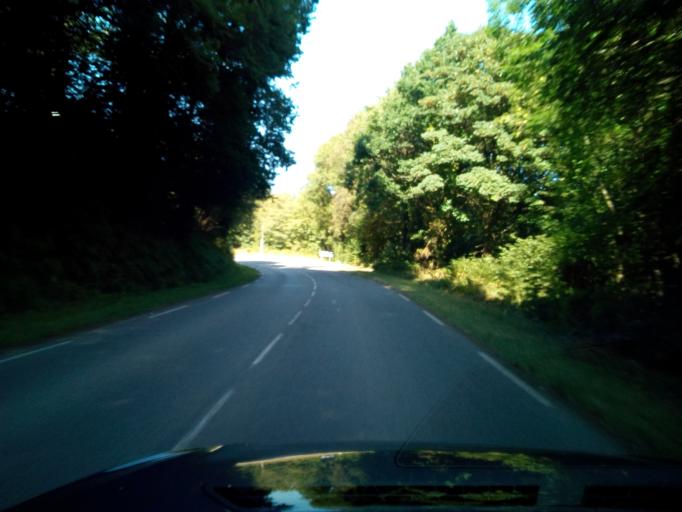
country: FR
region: Brittany
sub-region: Departement du Finistere
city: La Roche-Maurice
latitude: 48.4837
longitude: -4.1773
